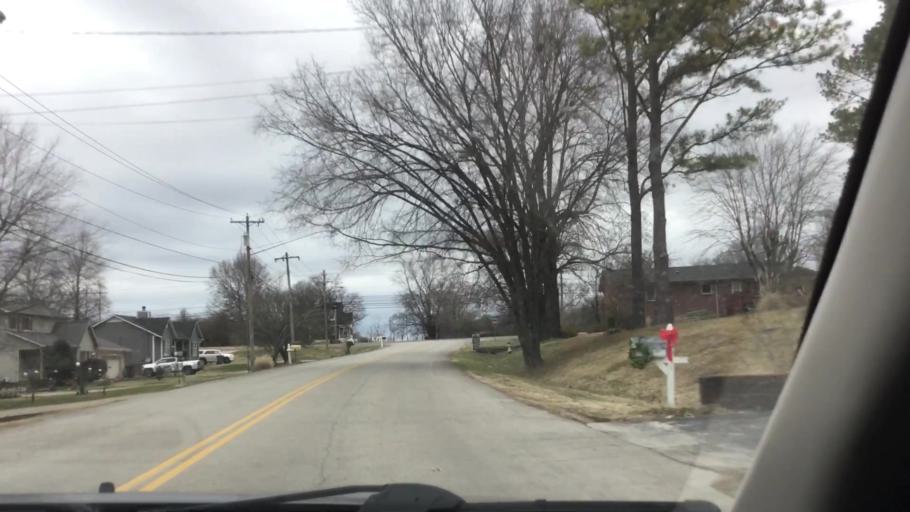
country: US
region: Tennessee
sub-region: Maury County
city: Columbia
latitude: 35.6238
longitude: -87.0967
